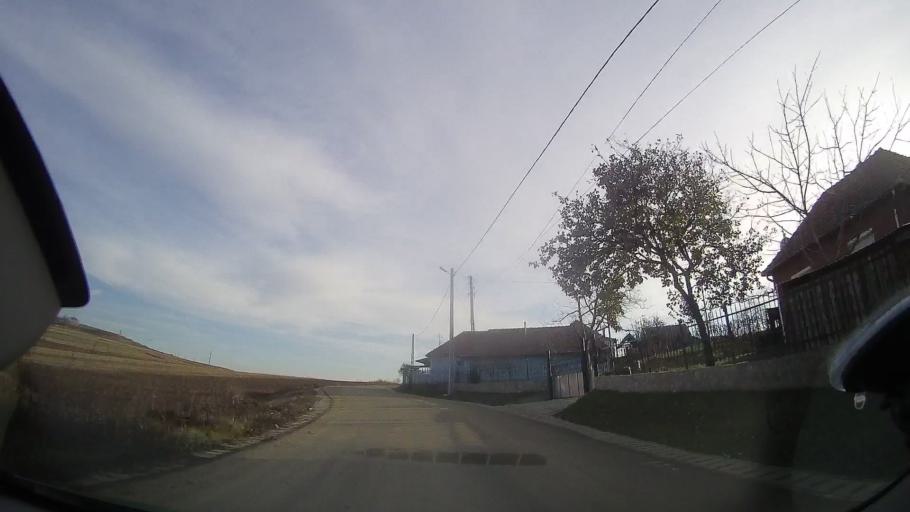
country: RO
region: Bihor
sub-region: Comuna Tileagd
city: Tileagd
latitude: 47.1003
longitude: 22.1756
